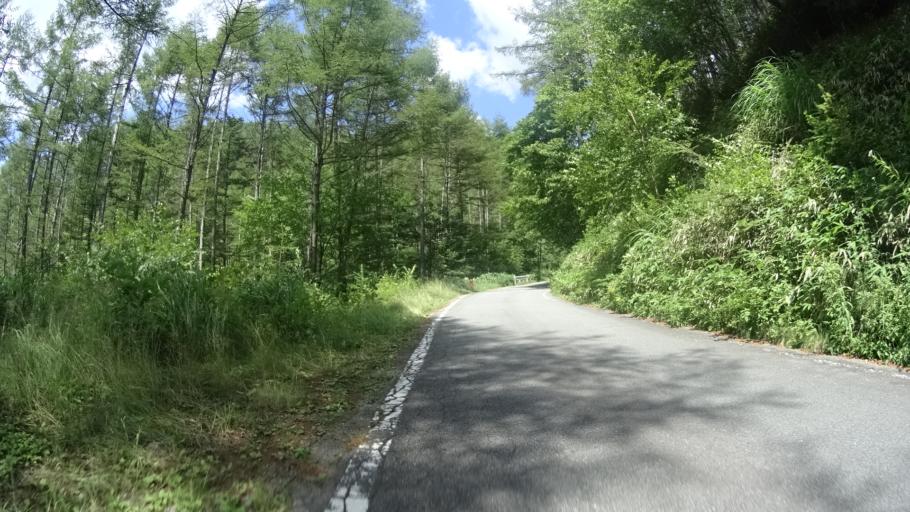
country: JP
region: Yamanashi
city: Enzan
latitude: 35.8261
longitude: 138.6453
